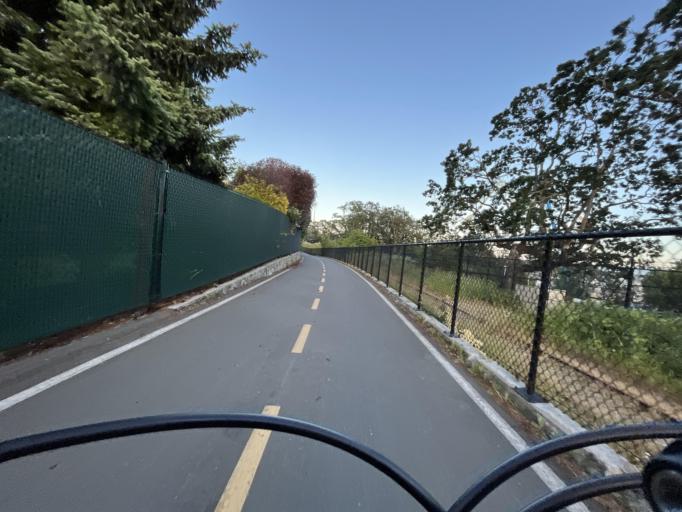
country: CA
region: British Columbia
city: Victoria
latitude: 48.4381
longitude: -123.4272
